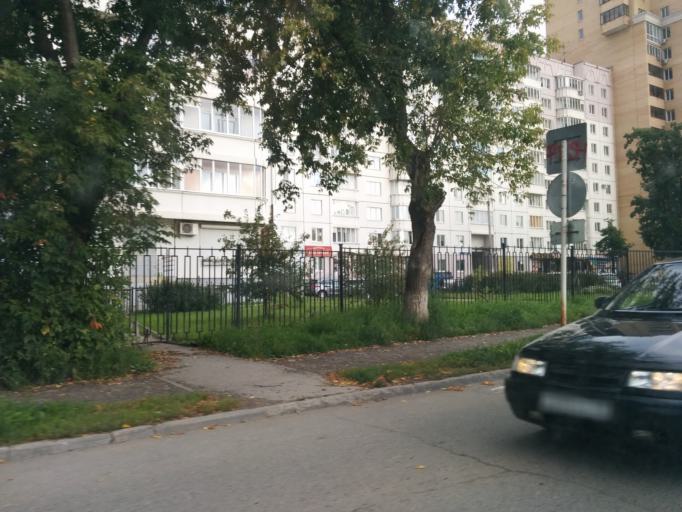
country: RU
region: Perm
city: Perm
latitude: 58.0020
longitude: 56.2987
